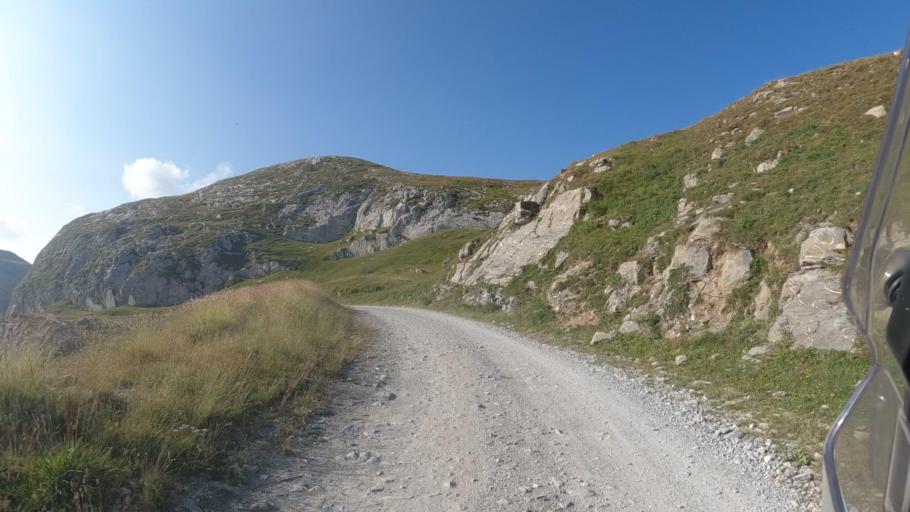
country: IT
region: Piedmont
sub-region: Provincia di Cuneo
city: Limone Piemonte
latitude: 44.1703
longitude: 7.6537
